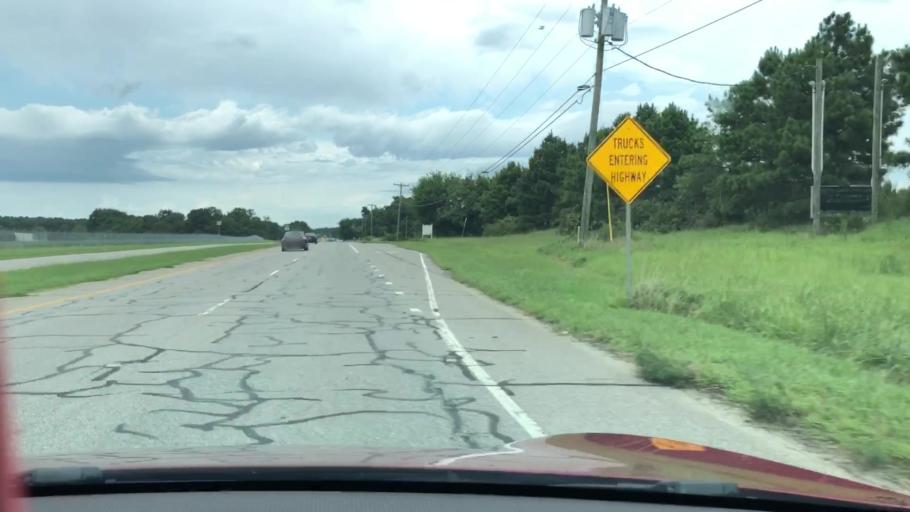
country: US
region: Virginia
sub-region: City of Virginia Beach
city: Virginia Beach
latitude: 36.8218
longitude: -76.0085
